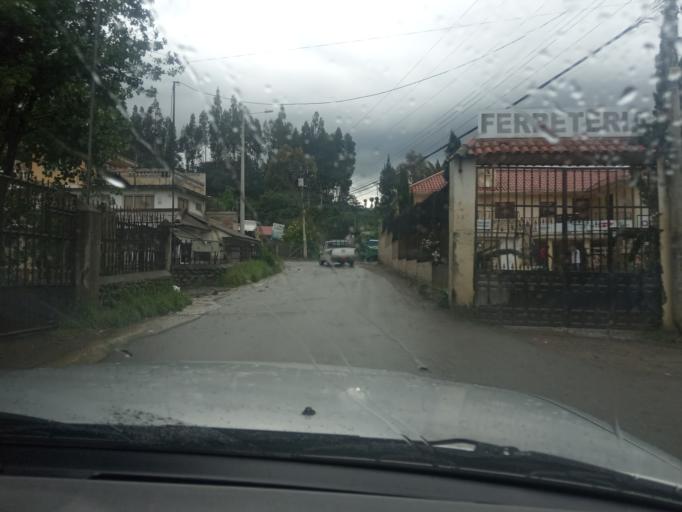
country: EC
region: Azuay
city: Llacao
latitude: -2.8618
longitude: -78.9369
